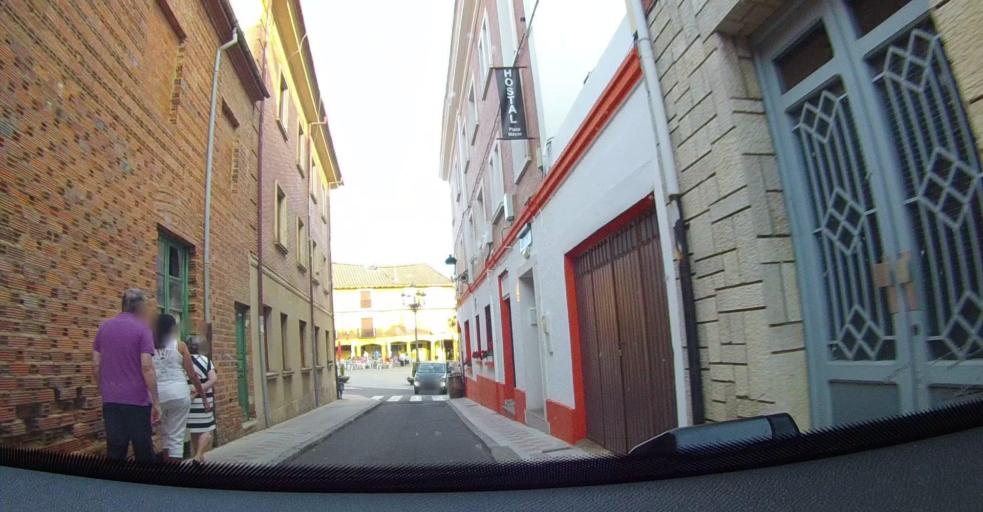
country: ES
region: Castille and Leon
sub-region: Provincia de Palencia
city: Carrion de los Condes
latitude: 42.3383
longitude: -4.6044
